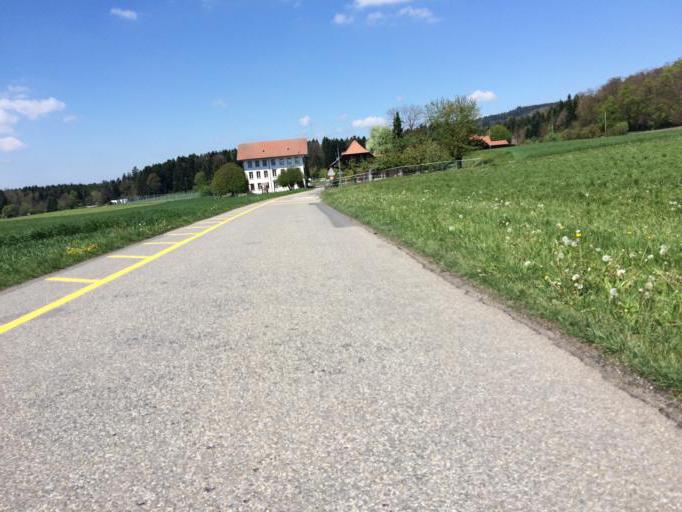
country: CH
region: Bern
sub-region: Bern-Mittelland District
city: Rubigen
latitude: 46.9203
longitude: 7.5425
